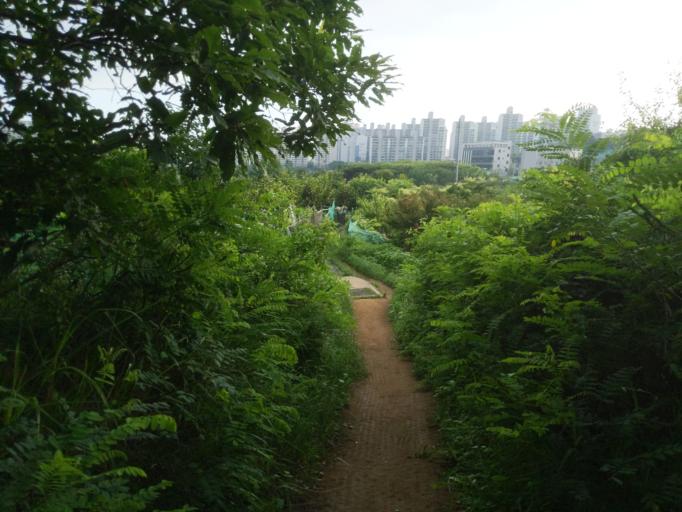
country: KR
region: Daegu
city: Hwawon
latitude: 35.8014
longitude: 128.5272
